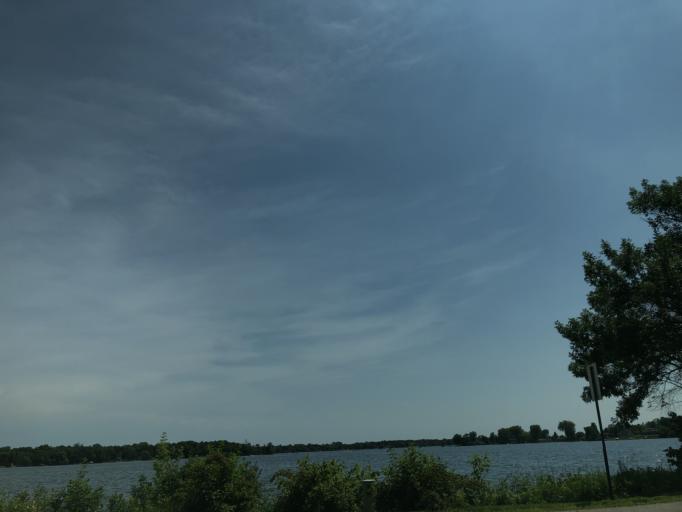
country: US
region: Minnesota
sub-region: Douglas County
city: Alexandria
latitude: 45.9327
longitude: -95.3829
